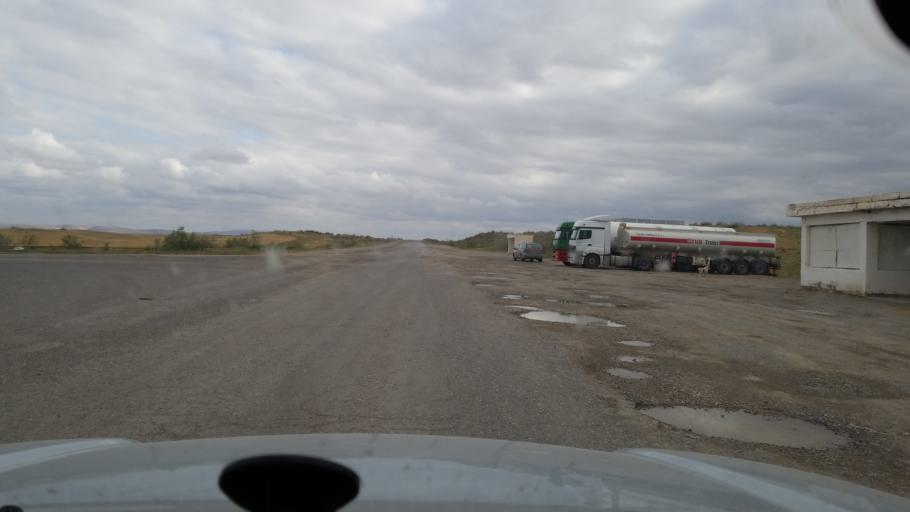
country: TM
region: Mary
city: Serhetabat
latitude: 35.9856
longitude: 62.6270
